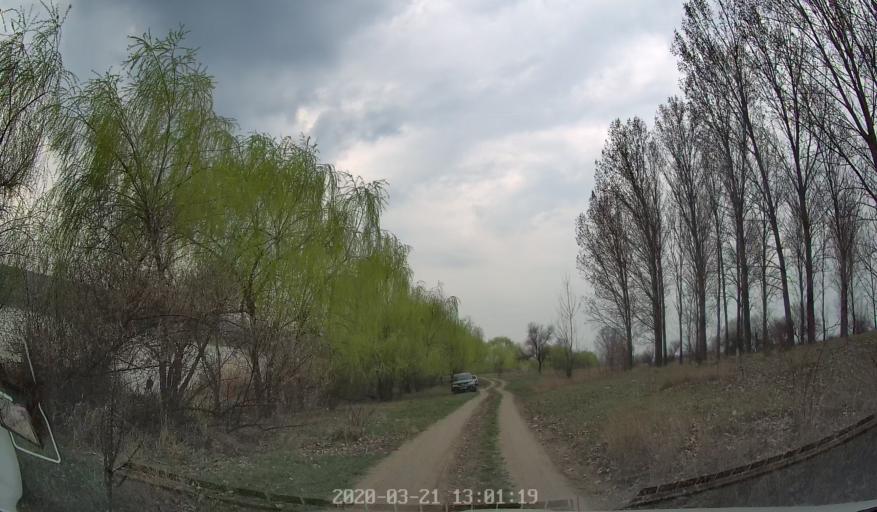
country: MD
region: Laloveni
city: Ialoveni
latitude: 46.9611
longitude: 28.7330
